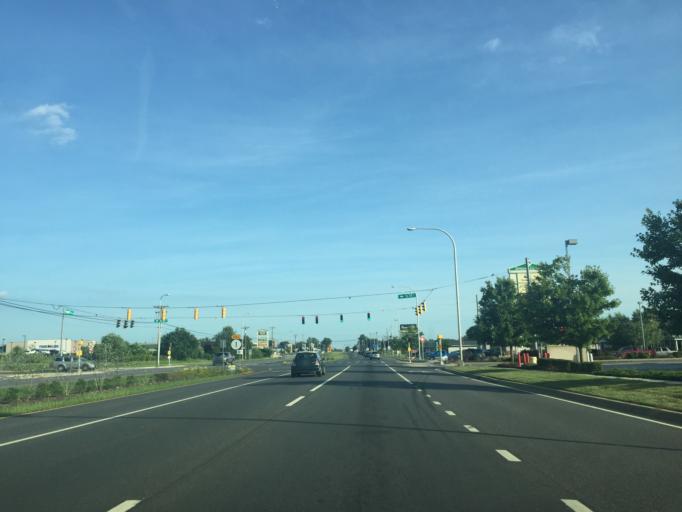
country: US
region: Delaware
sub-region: Kent County
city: Smyrna
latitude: 39.2824
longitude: -75.5936
